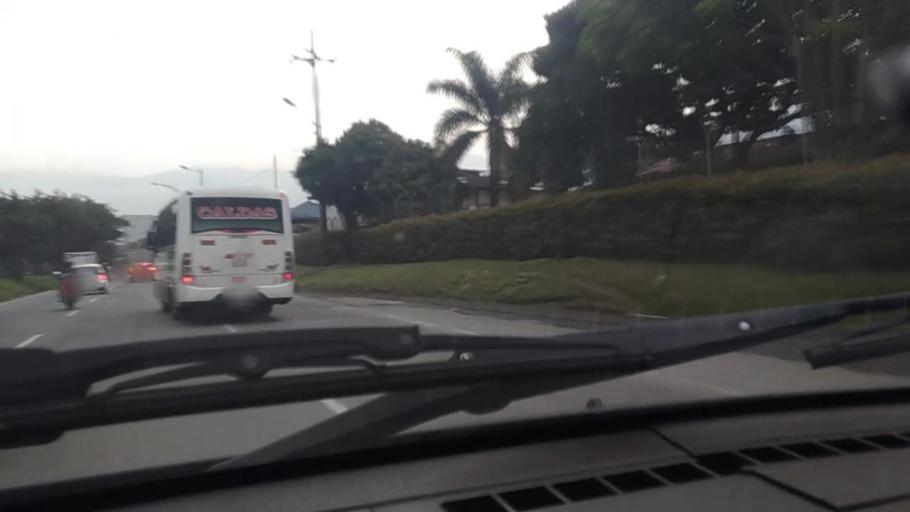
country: CO
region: Antioquia
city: Sabaneta
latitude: 6.1560
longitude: -75.6201
